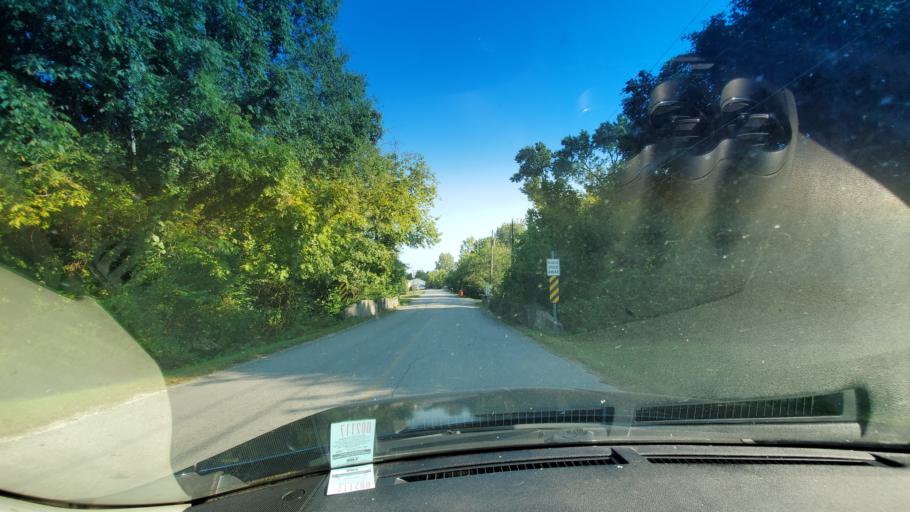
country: US
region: Tennessee
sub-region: Smith County
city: Carthage
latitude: 36.2541
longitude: -85.9567
